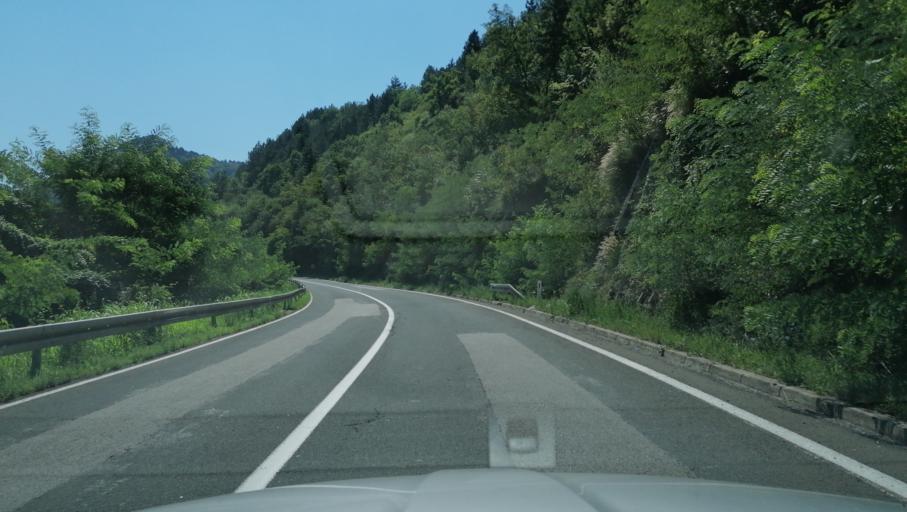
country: RS
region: Central Serbia
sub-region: Raski Okrug
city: Kraljevo
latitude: 43.6312
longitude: 20.5424
